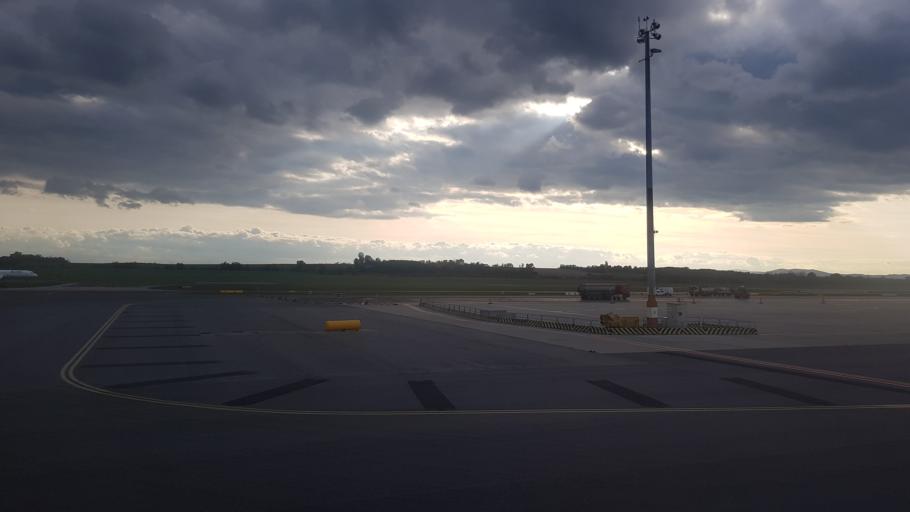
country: AT
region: Lower Austria
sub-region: Politischer Bezirk Wien-Umgebung
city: Fischamend Dorf
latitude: 48.1143
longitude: 16.5736
